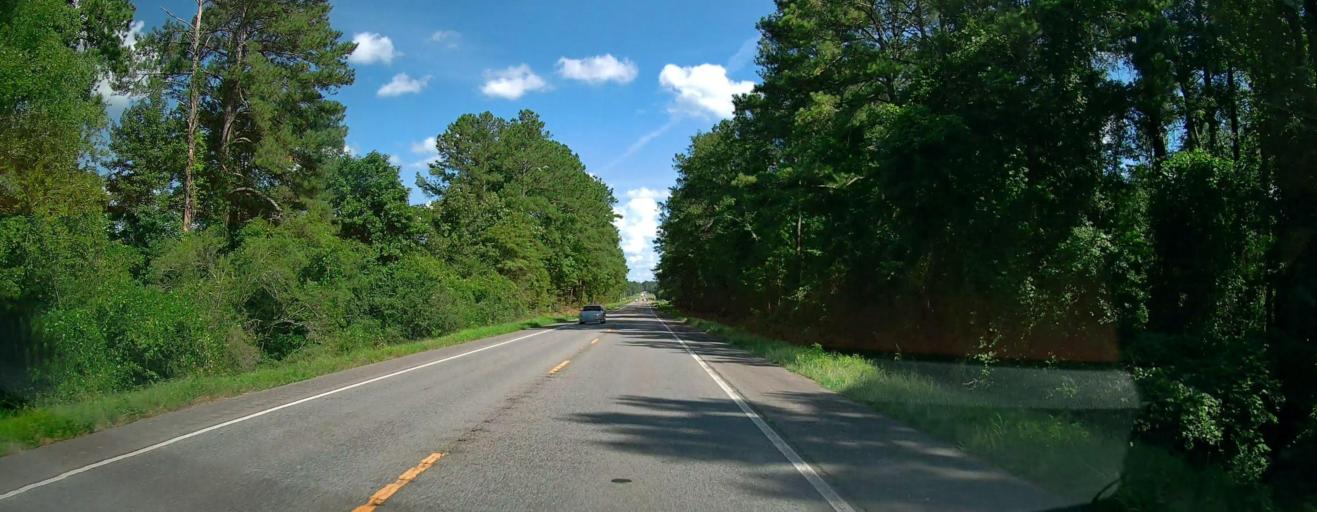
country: US
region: Alabama
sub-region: Pickens County
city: Gordo
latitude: 33.3071
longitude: -87.8873
